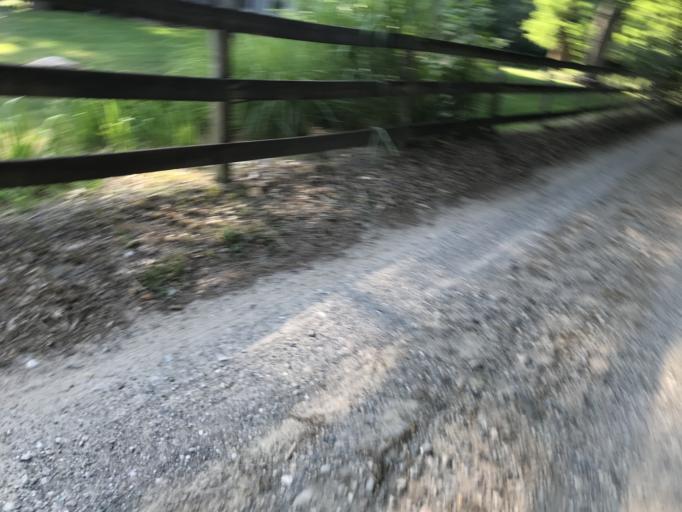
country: US
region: Michigan
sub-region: Oakland County
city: Farmington
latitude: 42.4693
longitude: -83.3839
